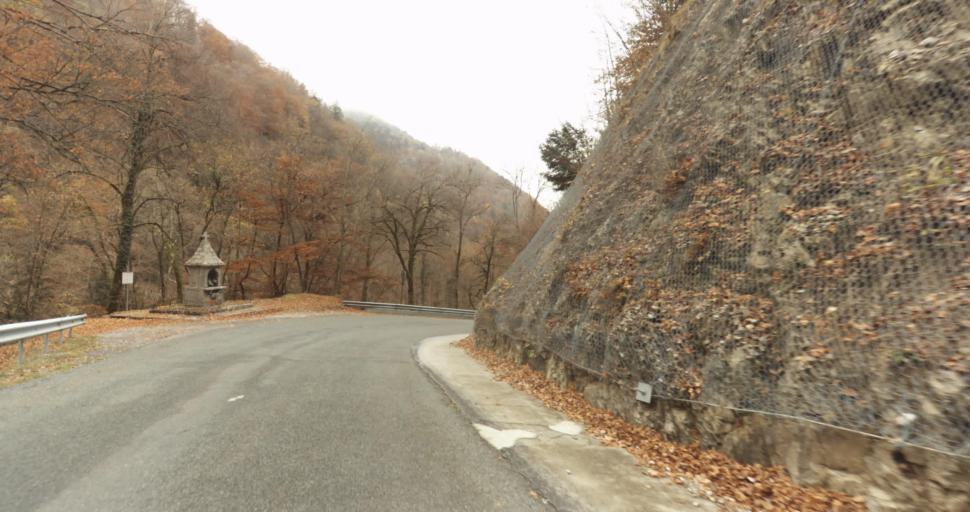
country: FR
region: Rhone-Alpes
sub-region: Departement de la Haute-Savoie
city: Doussard
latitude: 45.7797
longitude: 6.2601
